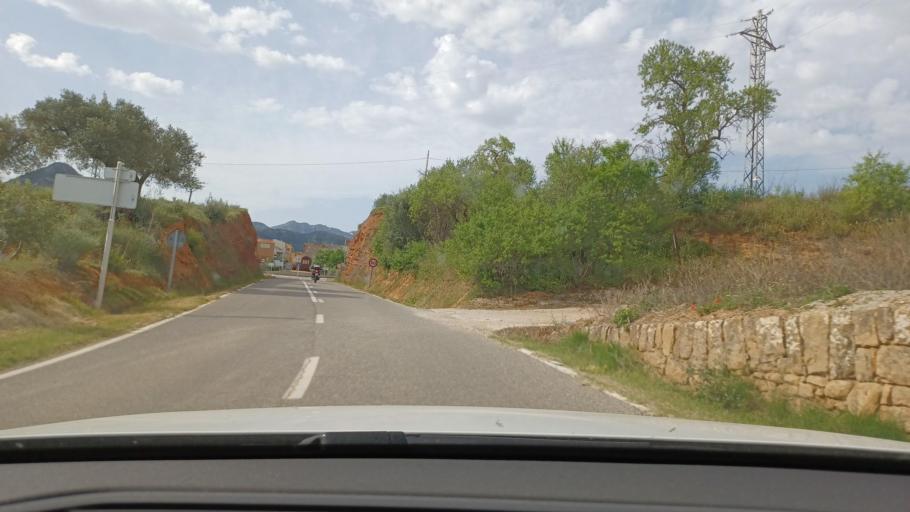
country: ES
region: Catalonia
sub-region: Provincia de Tarragona
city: Bot
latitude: 41.0131
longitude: 0.3852
